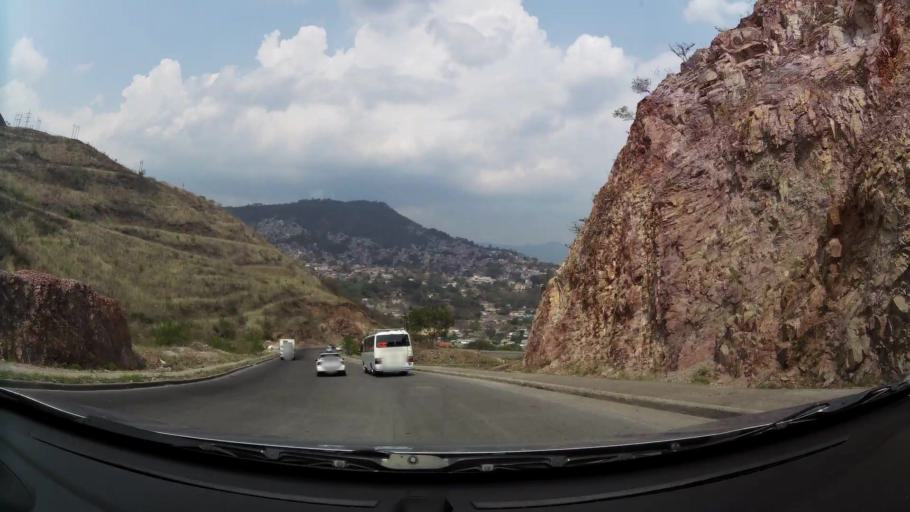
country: HN
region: Francisco Morazan
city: Tegucigalpa
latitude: 14.1137
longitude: -87.2156
